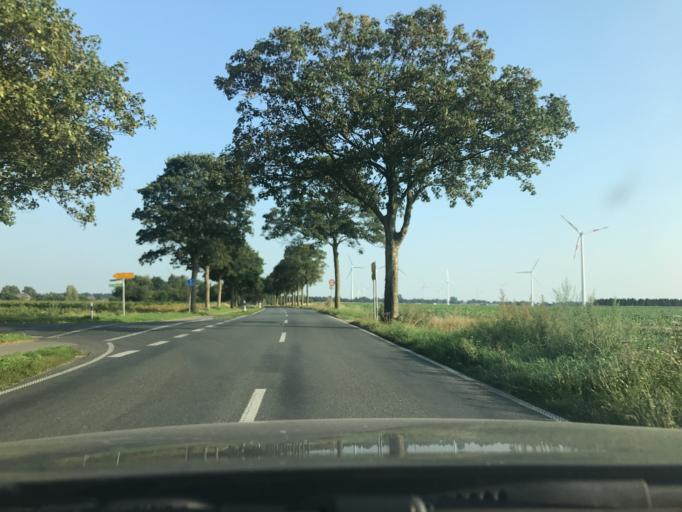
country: DE
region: North Rhine-Westphalia
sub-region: Regierungsbezirk Dusseldorf
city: Goch
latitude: 51.7205
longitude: 6.2192
